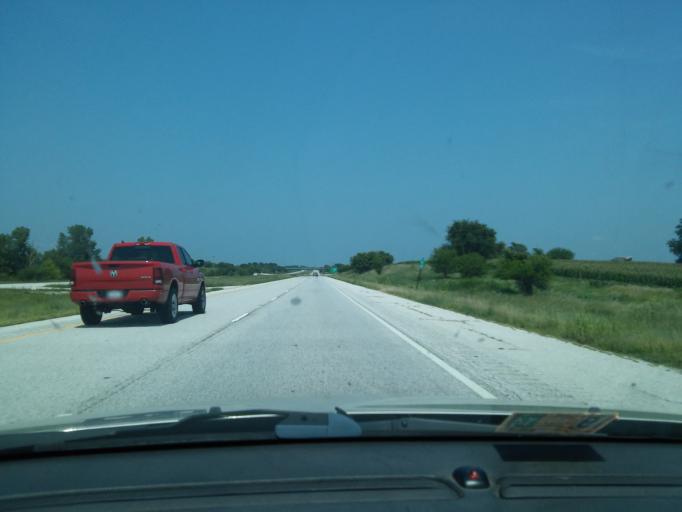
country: US
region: Illinois
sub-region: Morgan County
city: South Jacksonville
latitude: 39.7156
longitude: -90.1751
